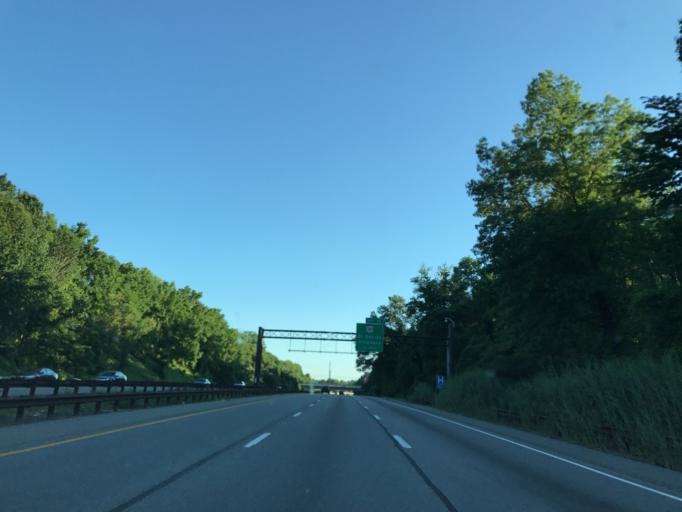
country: US
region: Pennsylvania
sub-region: Delaware County
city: Radnor
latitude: 40.0468
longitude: -75.3487
